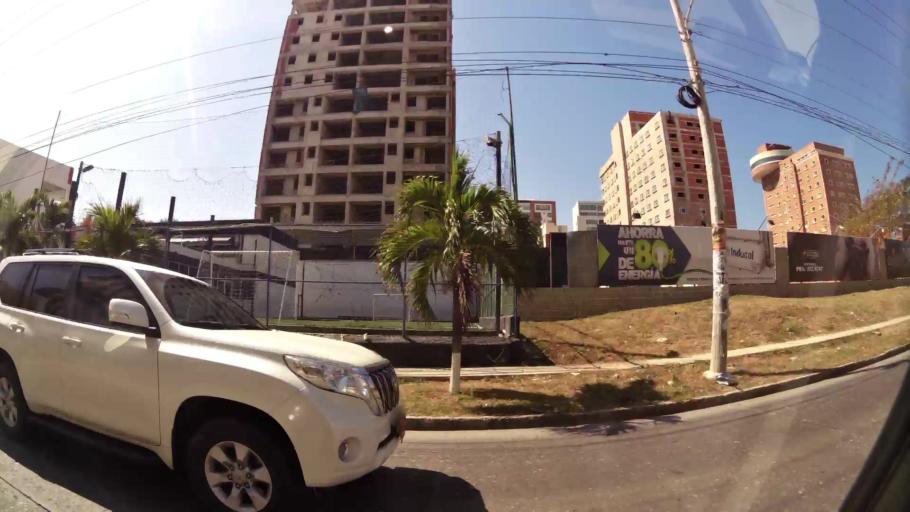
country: CO
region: Atlantico
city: Barranquilla
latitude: 11.0135
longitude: -74.8255
